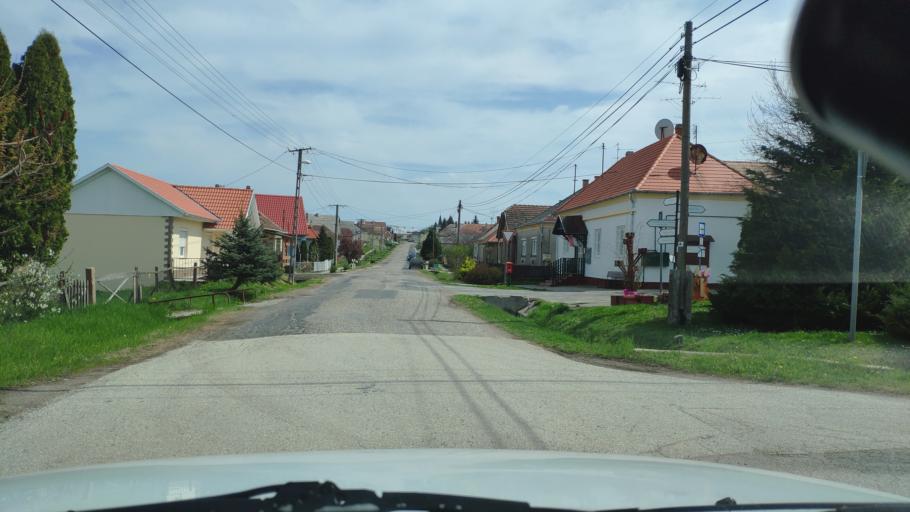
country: HU
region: Zala
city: Nagykanizsa
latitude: 46.4239
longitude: 17.0260
